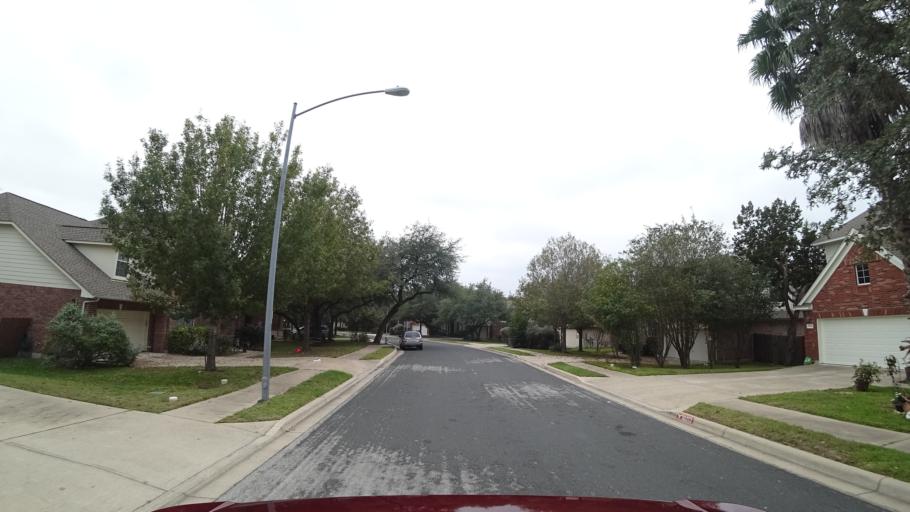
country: US
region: Texas
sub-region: Williamson County
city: Anderson Mill
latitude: 30.4314
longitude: -97.8194
